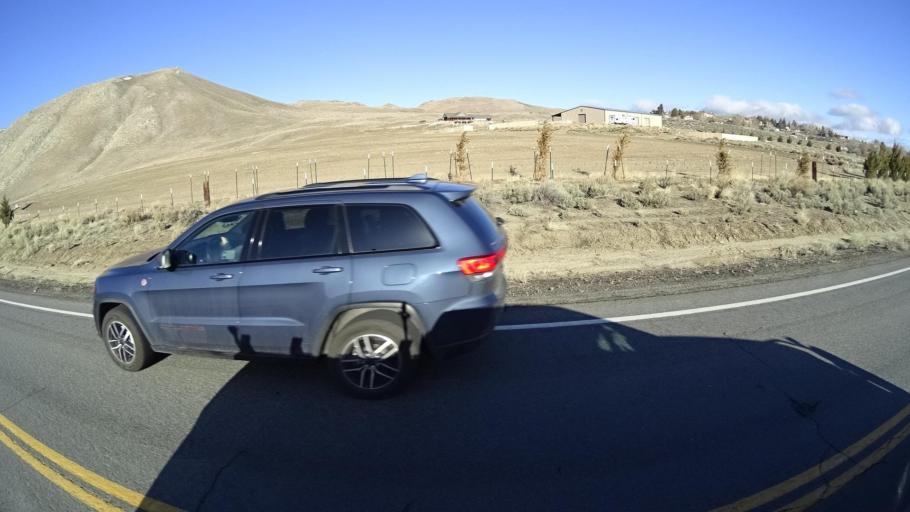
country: US
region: Nevada
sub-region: Washoe County
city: Cold Springs
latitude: 39.6532
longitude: -119.9229
